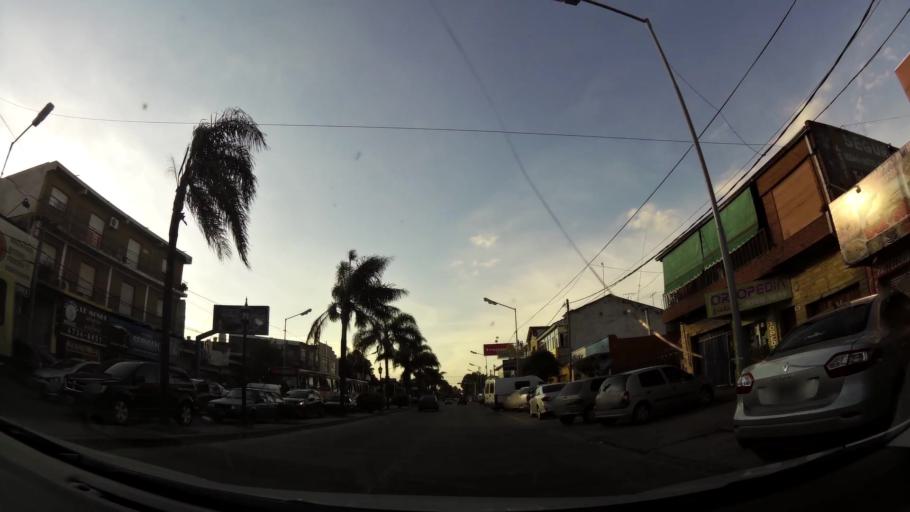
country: AR
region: Buenos Aires
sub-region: Partido de Tigre
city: Tigre
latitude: -34.4594
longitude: -58.6361
